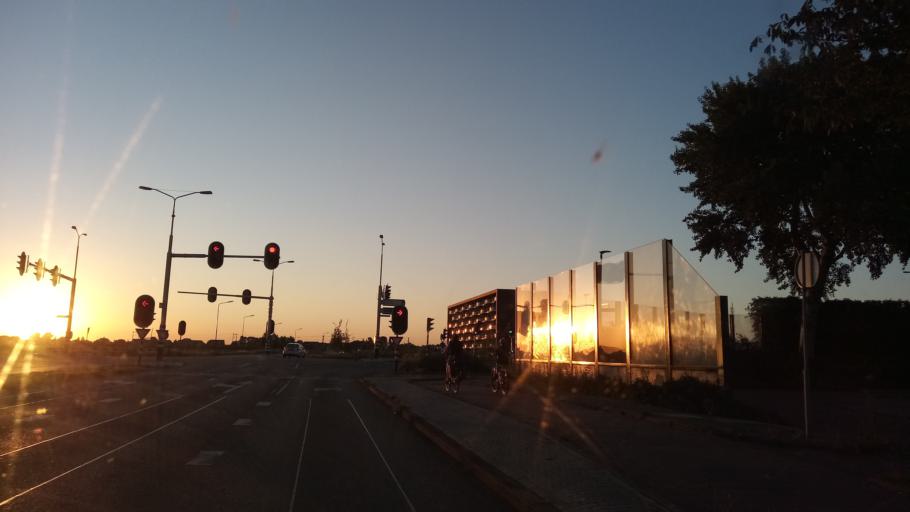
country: NL
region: North Holland
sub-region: Gemeente Langedijk
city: Broek op Langedijk
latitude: 52.6592
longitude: 4.8106
